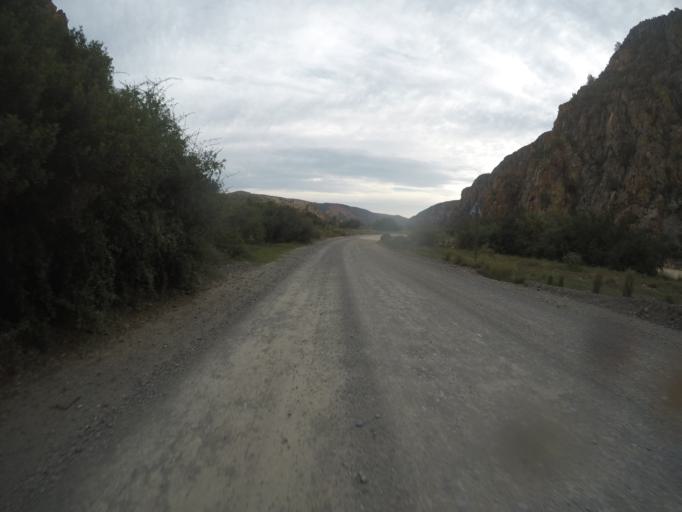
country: ZA
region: Eastern Cape
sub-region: Cacadu District Municipality
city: Willowmore
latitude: -33.5193
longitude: 23.6742
